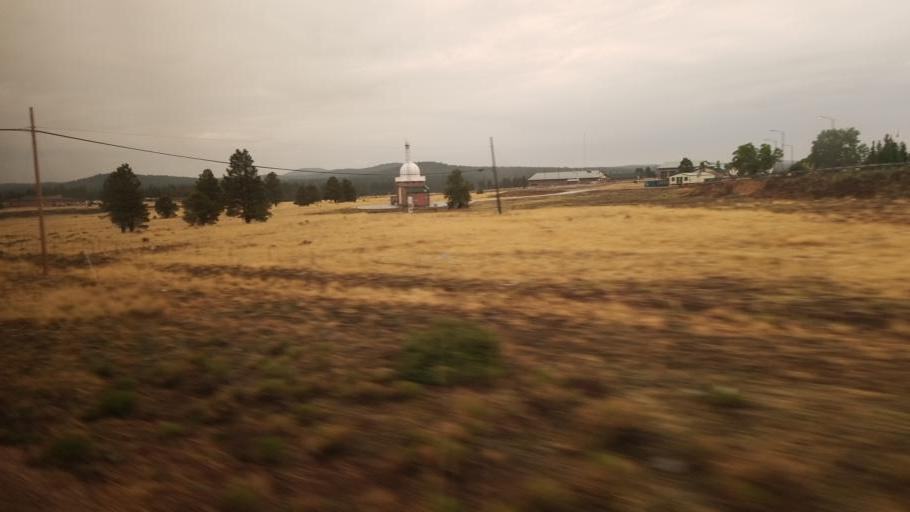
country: US
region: Arizona
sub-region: Coconino County
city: Parks
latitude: 35.2320
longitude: -111.8210
